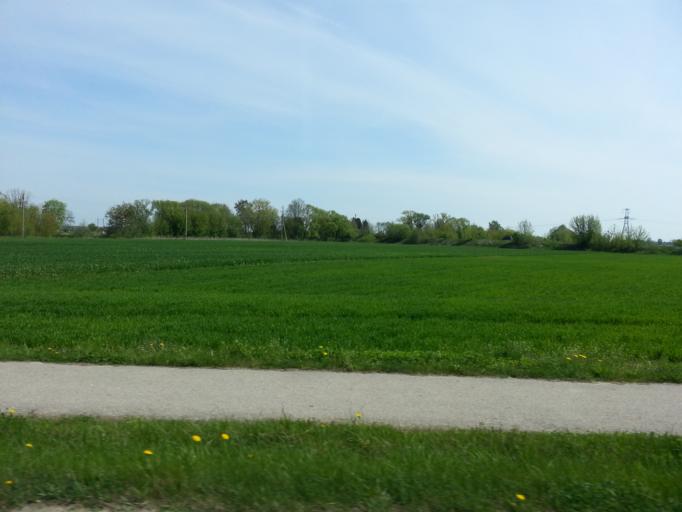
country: LT
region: Panevezys
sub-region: Panevezys City
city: Panevezys
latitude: 55.7888
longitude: 24.2847
